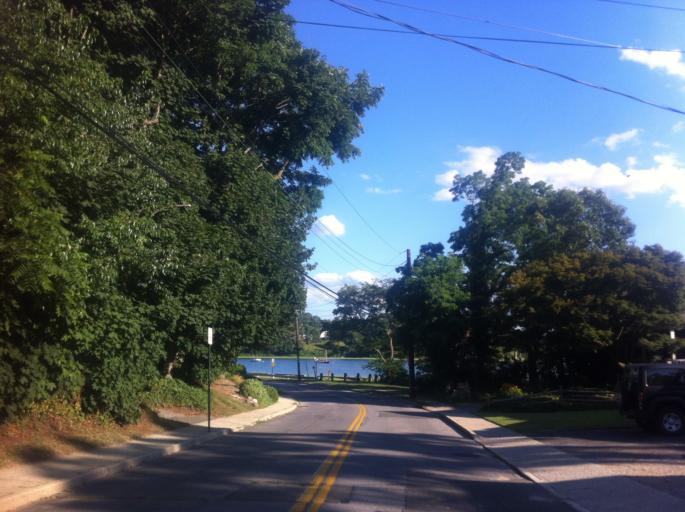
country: US
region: New York
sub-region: Nassau County
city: Bayville
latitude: 40.9011
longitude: -73.5690
